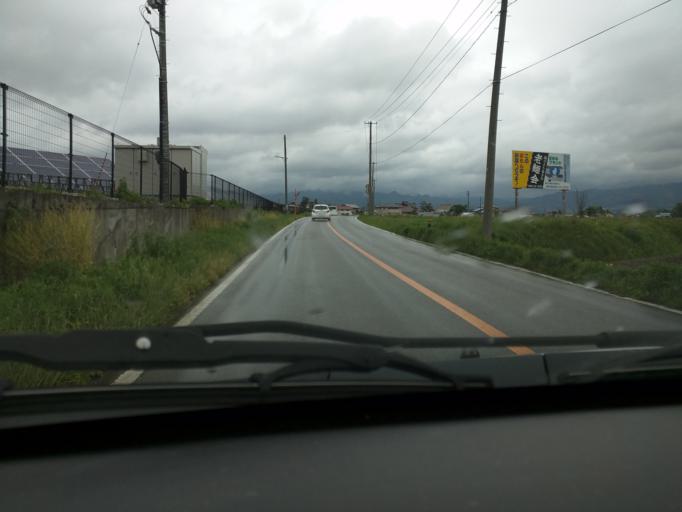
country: JP
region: Fukushima
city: Kitakata
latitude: 37.6221
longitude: 139.8666
